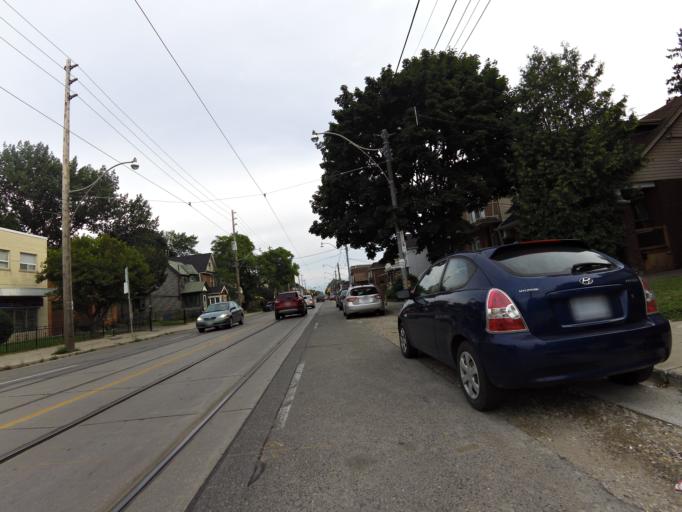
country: CA
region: Ontario
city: Toronto
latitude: 43.6679
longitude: -79.3173
